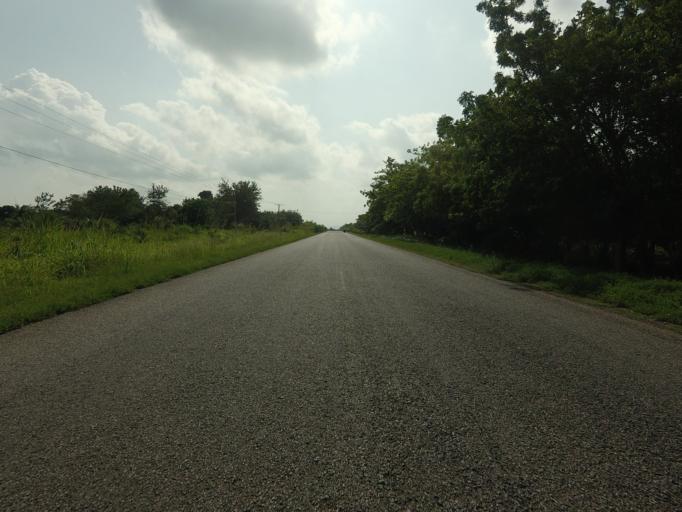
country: GH
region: Volta
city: Ho
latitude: 6.5795
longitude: 0.5810
